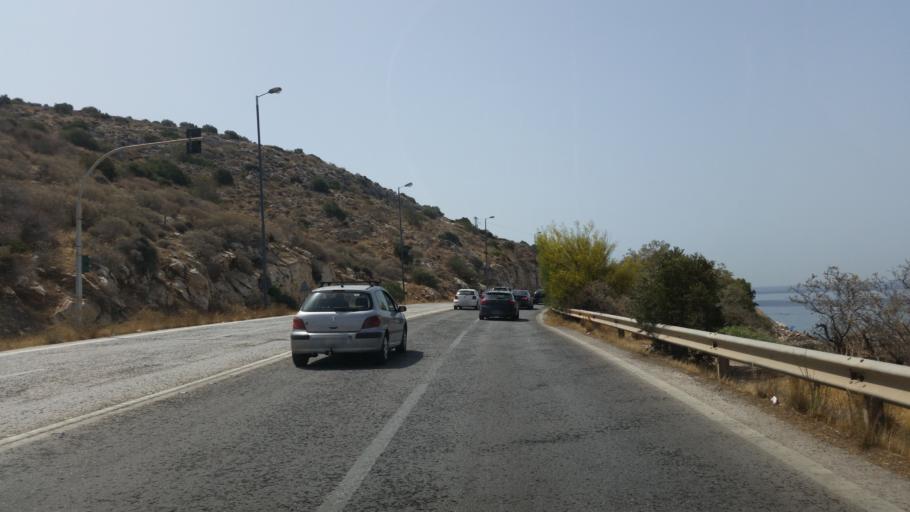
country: GR
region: Attica
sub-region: Nomarchia Anatolikis Attikis
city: Vouliagmeni
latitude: 37.8063
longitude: 23.7845
